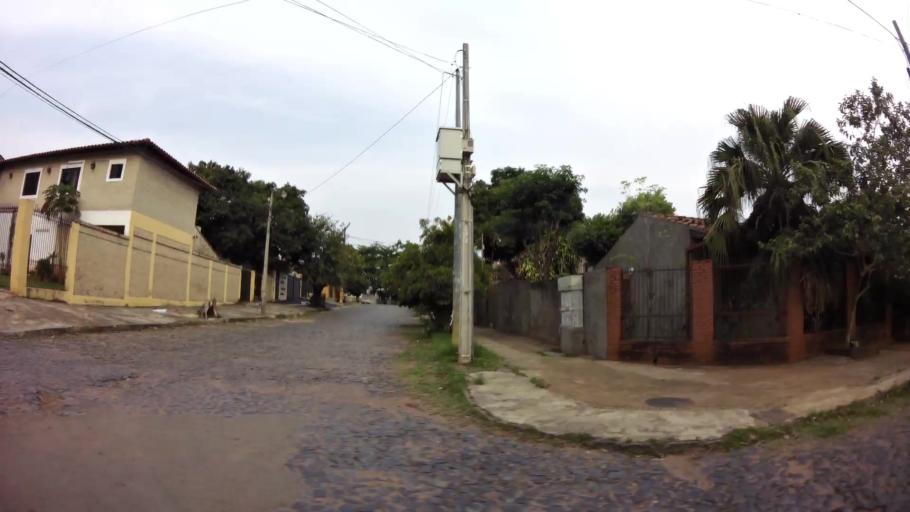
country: PY
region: Asuncion
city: Asuncion
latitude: -25.3107
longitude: -57.6065
